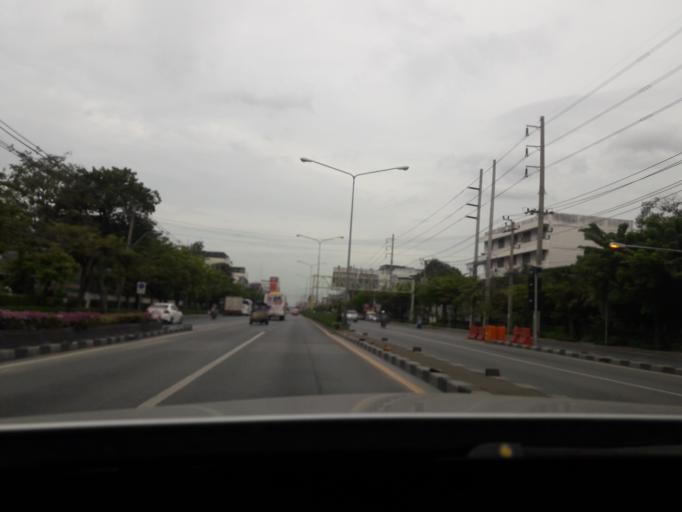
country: TH
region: Bangkok
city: Bang Phlat
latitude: 13.7856
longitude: 100.4917
